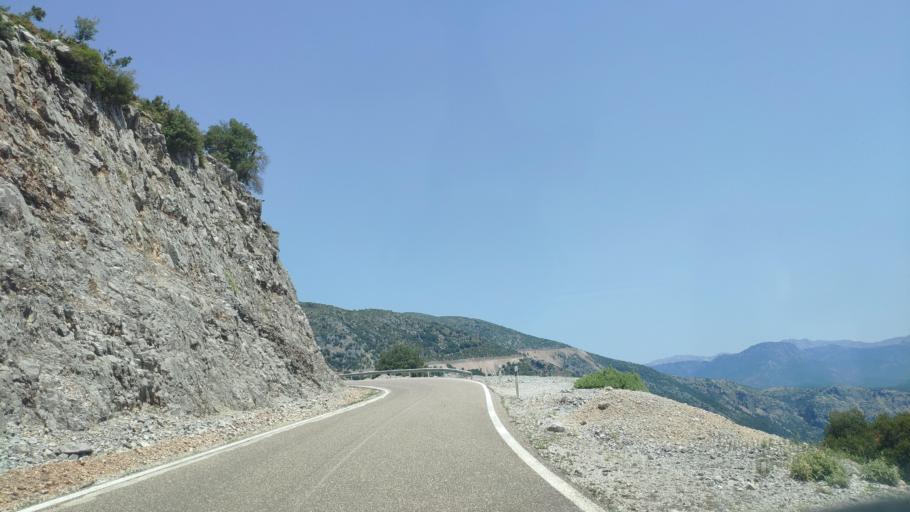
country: GR
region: West Greece
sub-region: Nomos Aitolias kai Akarnanias
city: Krikellos
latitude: 39.0234
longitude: 21.3704
